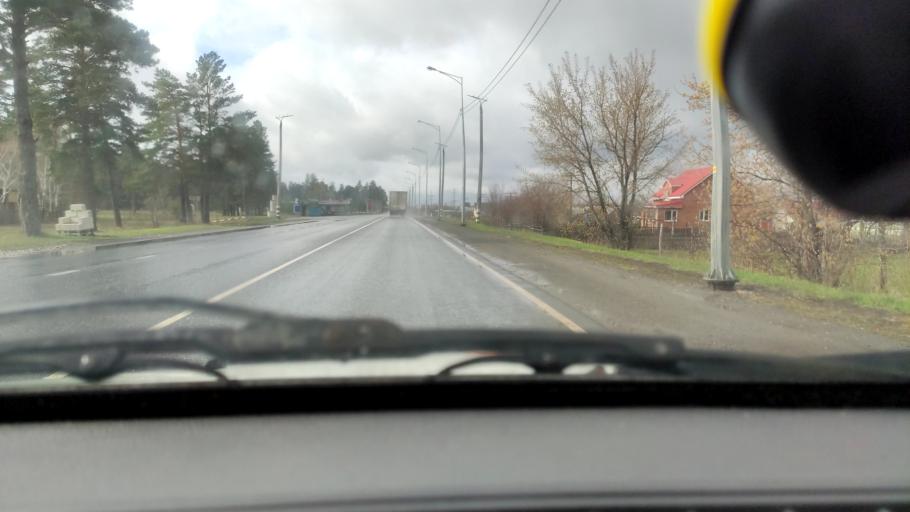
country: RU
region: Samara
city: Povolzhskiy
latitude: 53.5857
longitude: 49.5720
